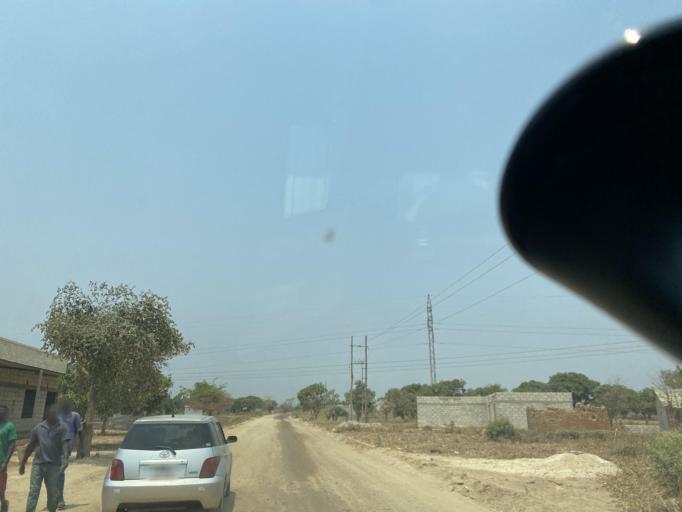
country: ZM
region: Lusaka
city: Lusaka
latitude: -15.5454
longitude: 28.3567
